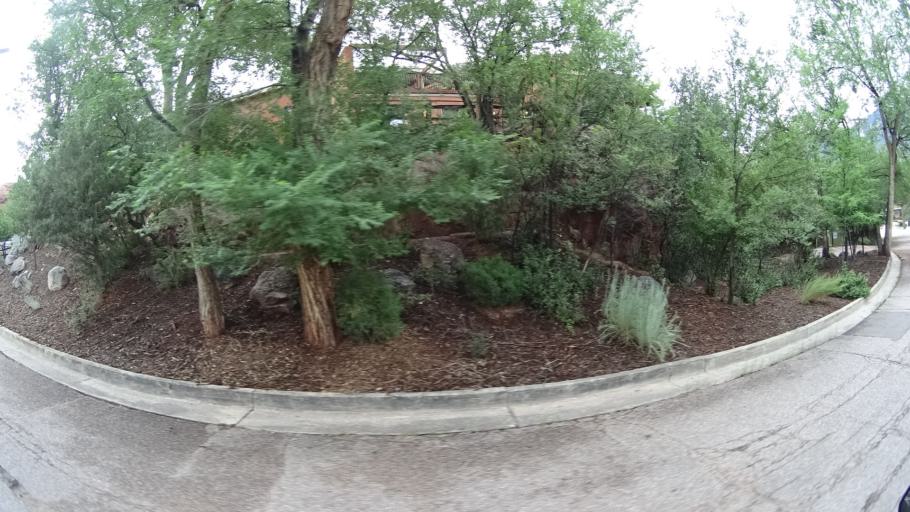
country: US
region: Colorado
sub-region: El Paso County
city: Manitou Springs
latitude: 38.8625
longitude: -104.8906
